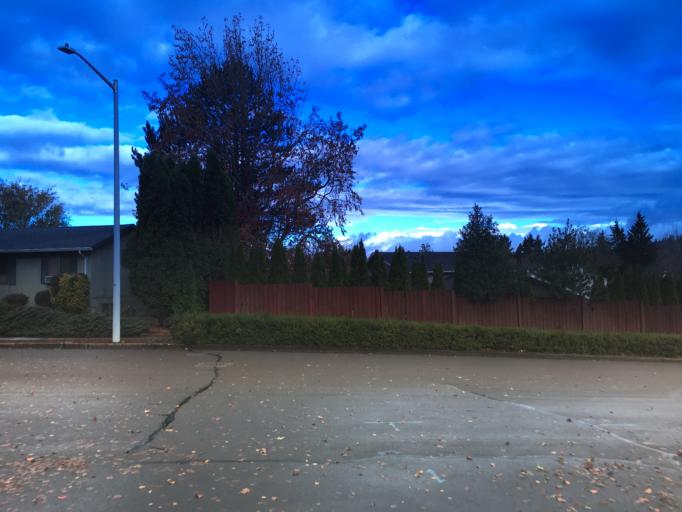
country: US
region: Oregon
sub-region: Multnomah County
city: Troutdale
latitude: 45.5202
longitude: -122.3787
